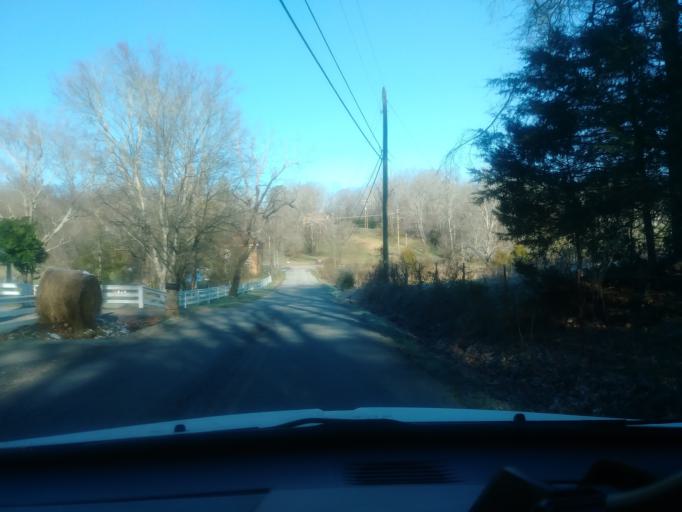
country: US
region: Tennessee
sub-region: Greene County
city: Mosheim
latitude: 36.1187
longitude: -82.9384
